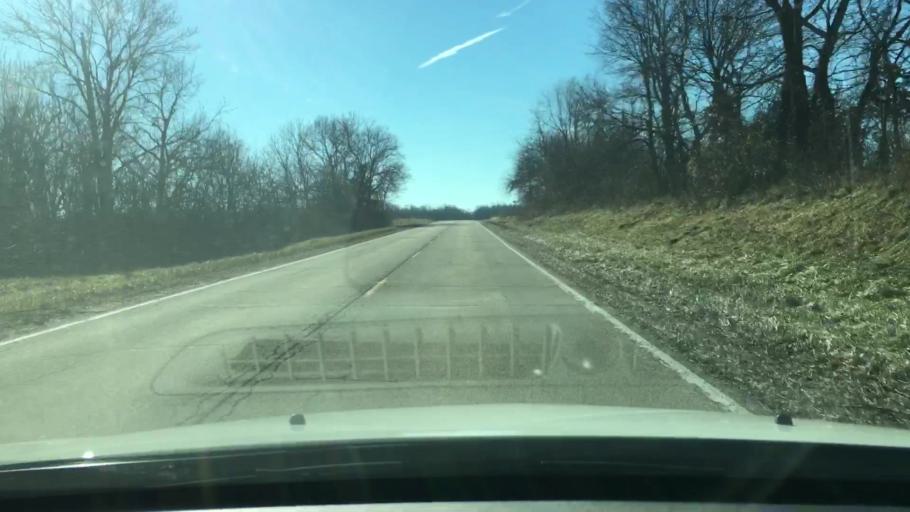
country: US
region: Illinois
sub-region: Mason County
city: Havana
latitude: 40.2946
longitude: -90.1529
